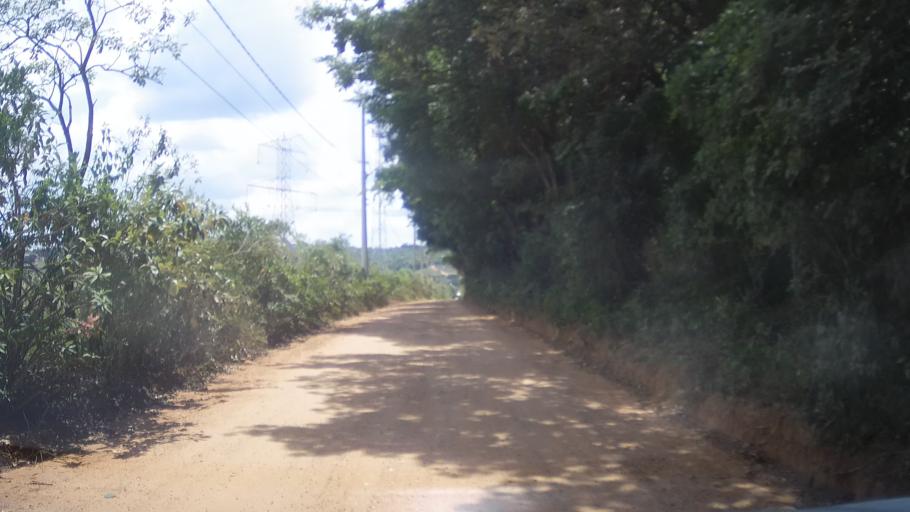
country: BR
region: Sao Paulo
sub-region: Itupeva
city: Itupeva
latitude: -23.1806
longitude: -47.0079
